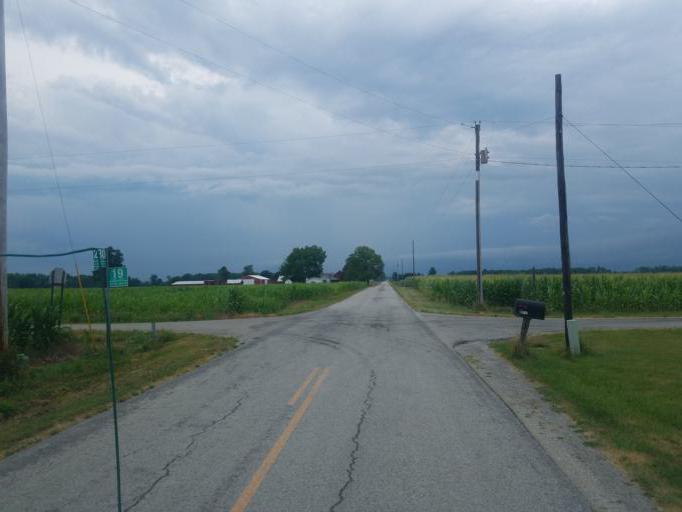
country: US
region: Ohio
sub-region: Defiance County
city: Hicksville
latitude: 41.2373
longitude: -84.7756
